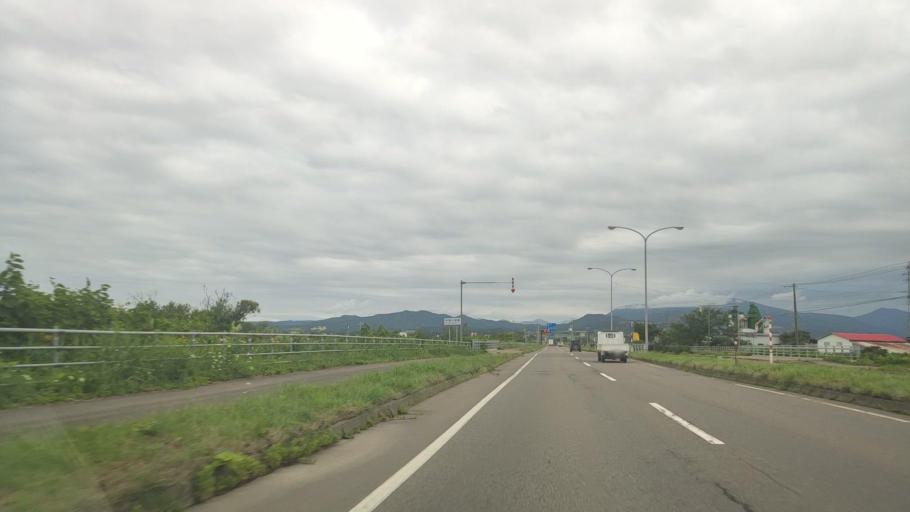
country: JP
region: Hokkaido
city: Nanae
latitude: 42.2717
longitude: 140.2725
